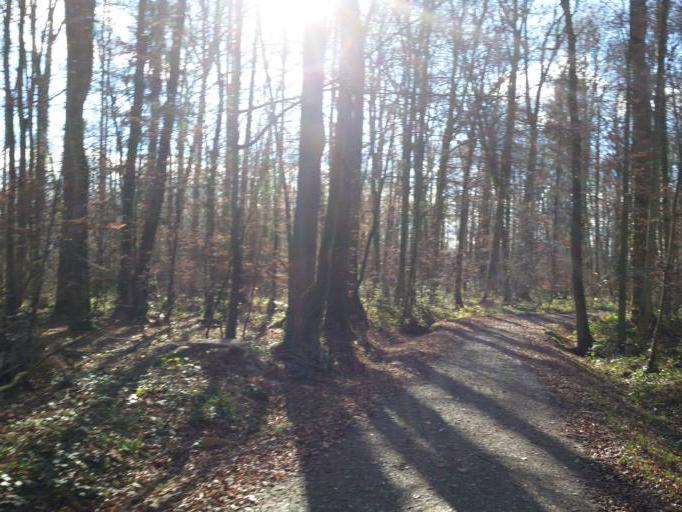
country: CH
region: Thurgau
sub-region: Arbon District
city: Uttwil
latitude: 47.5627
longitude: 9.3447
